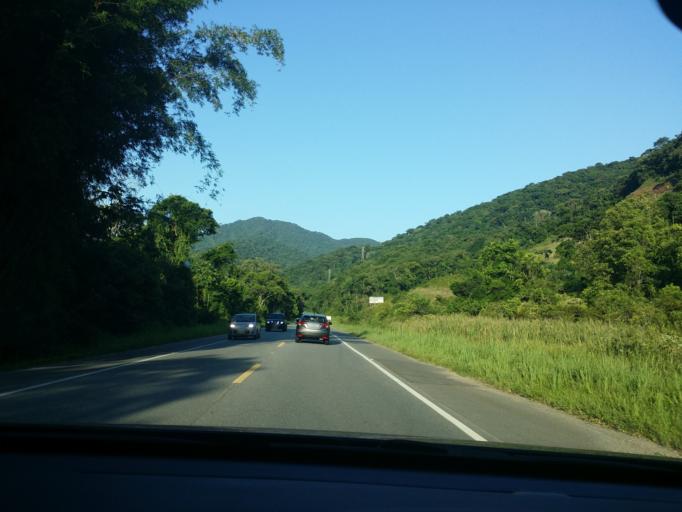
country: BR
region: Sao Paulo
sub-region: Sao Sebastiao
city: Sao Sebastiao
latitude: -23.7496
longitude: -45.7460
